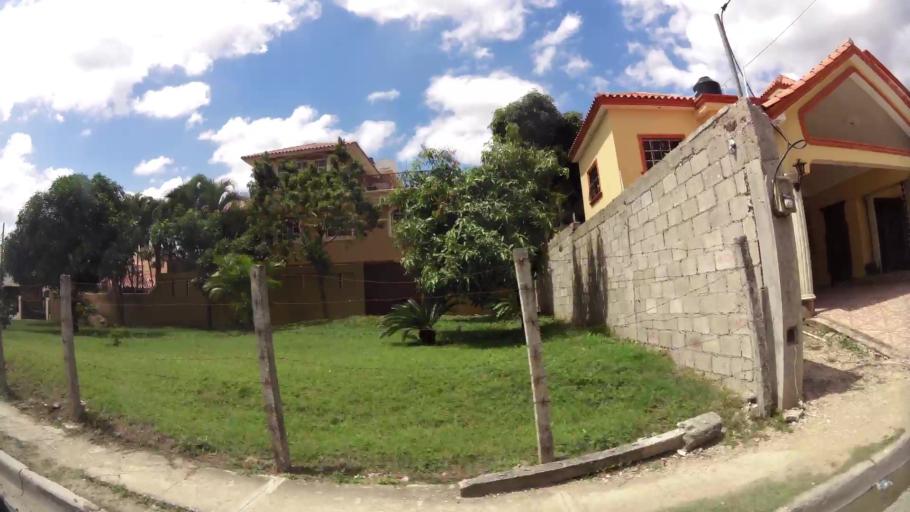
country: DO
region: San Cristobal
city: San Cristobal
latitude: 18.4106
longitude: -70.1030
